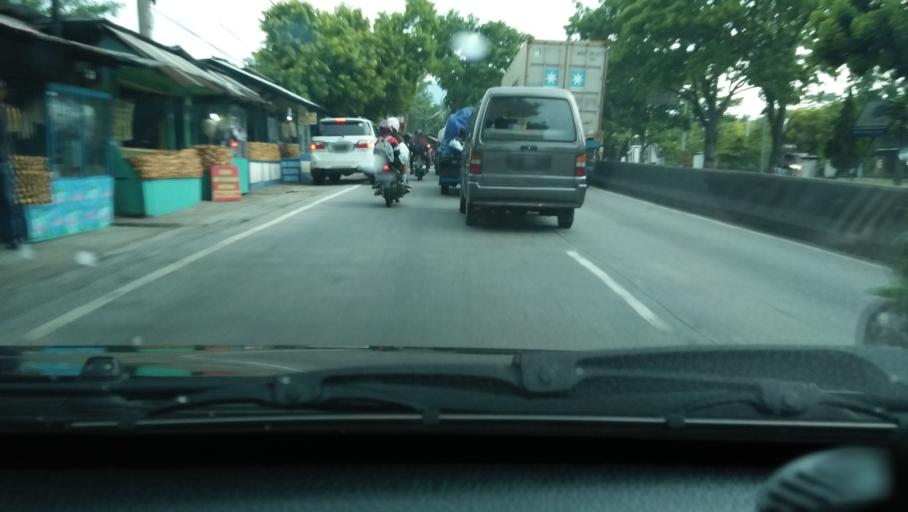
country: ID
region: Central Java
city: Ungaran
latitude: -7.0832
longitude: 110.4106
